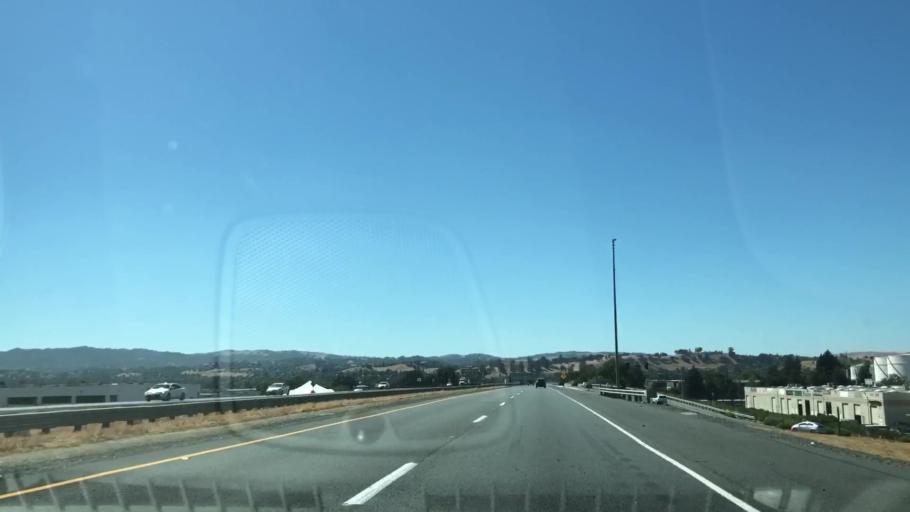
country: US
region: California
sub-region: Contra Costa County
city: Concord
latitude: 38.0021
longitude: -122.0494
